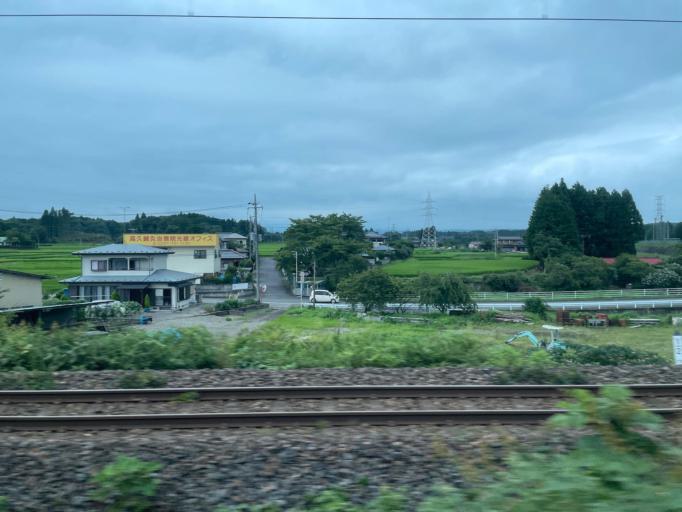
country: JP
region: Tochigi
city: Kuroiso
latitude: 37.0187
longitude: 140.1102
